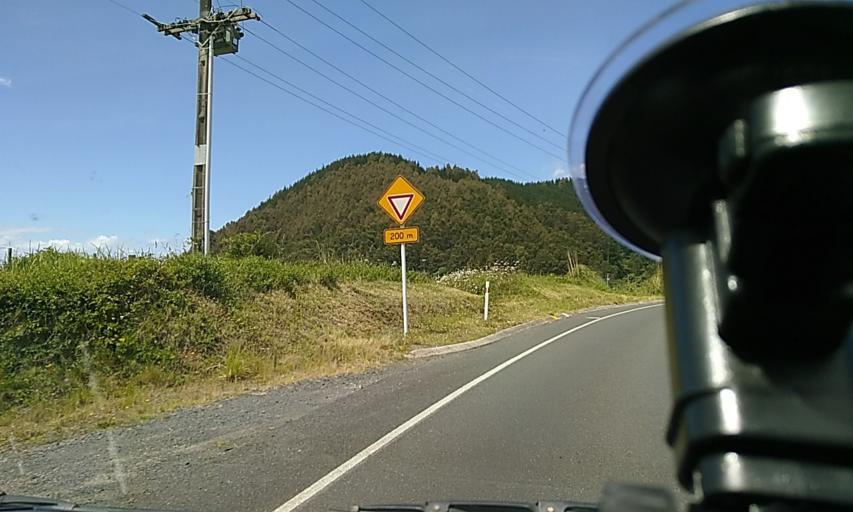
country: NZ
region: Bay of Plenty
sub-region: Western Bay of Plenty District
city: Waihi Beach
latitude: -37.4579
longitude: 175.9320
